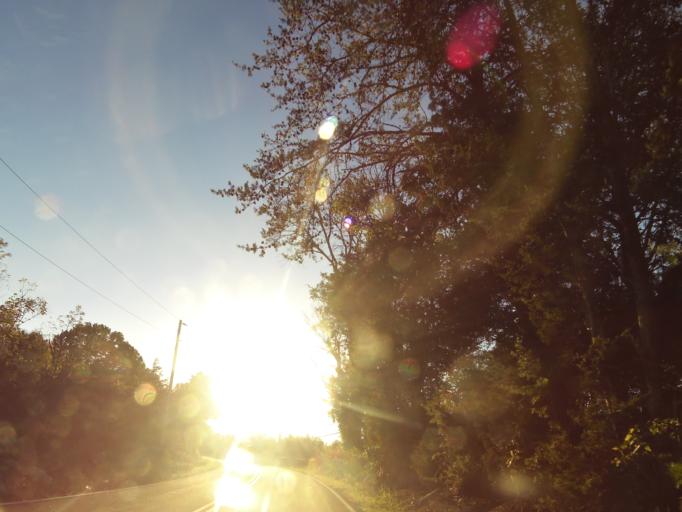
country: US
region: Tennessee
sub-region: Grainger County
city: Rutledge
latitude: 36.3064
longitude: -83.5622
